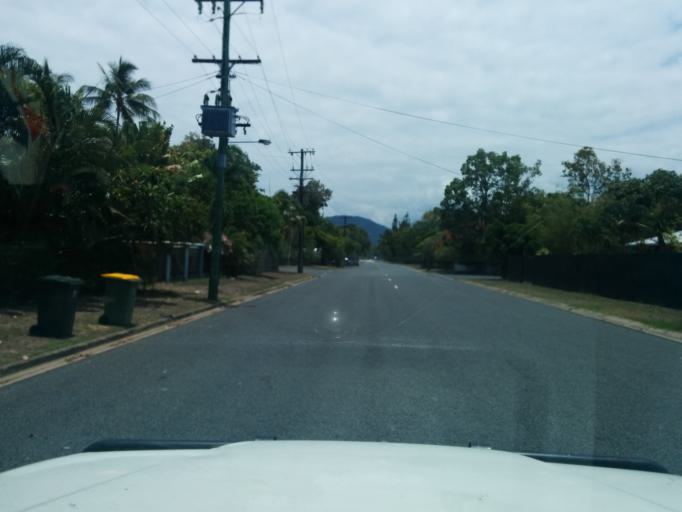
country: AU
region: Queensland
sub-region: Cairns
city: Yorkeys Knob
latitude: -16.8394
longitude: 145.7358
